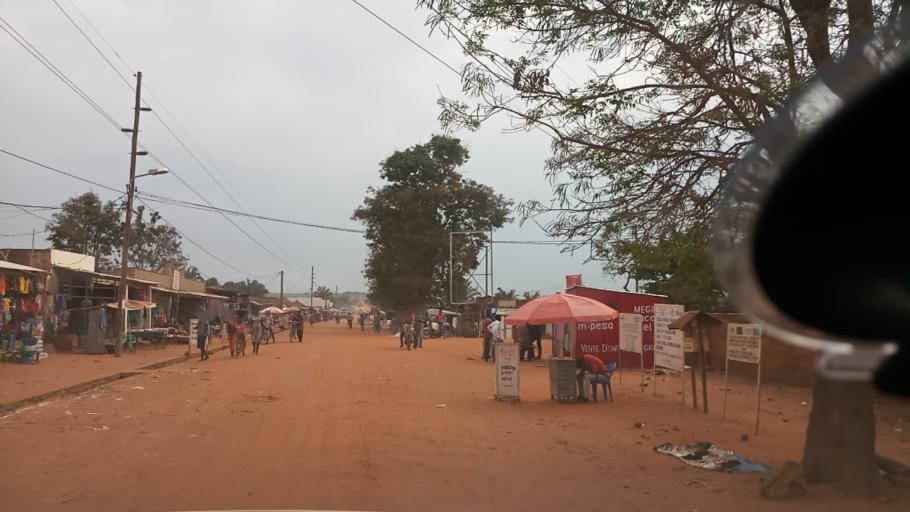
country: ZM
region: Northern
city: Kaputa
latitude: -8.4653
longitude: 28.8999
